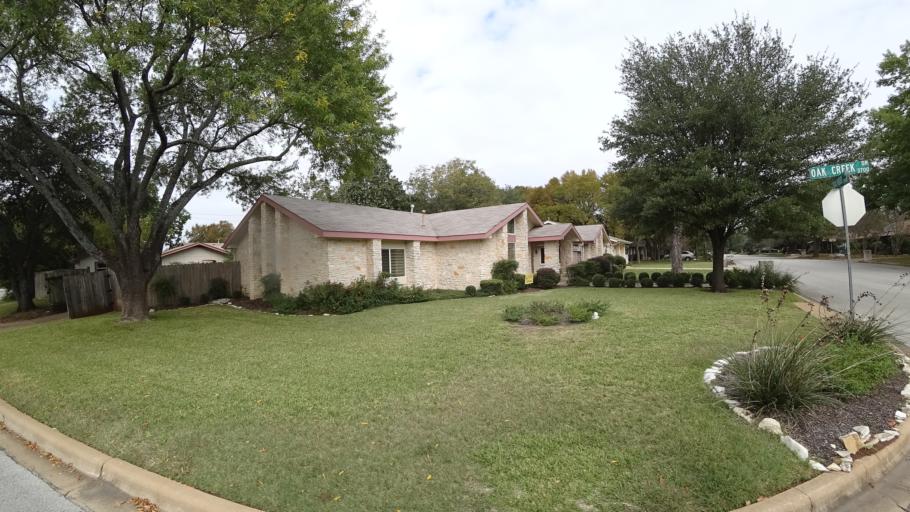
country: US
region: Texas
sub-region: Travis County
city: Wells Branch
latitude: 30.4277
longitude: -97.7087
